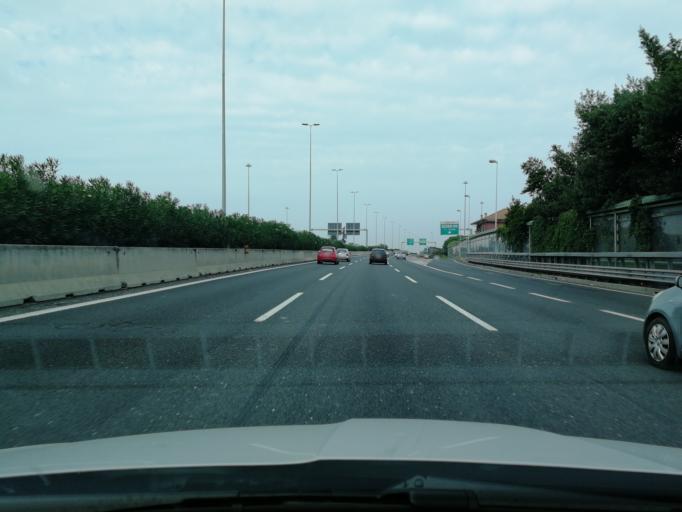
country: IT
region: Latium
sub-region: Citta metropolitana di Roma Capitale
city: Ciampino
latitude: 41.8619
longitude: 12.6000
